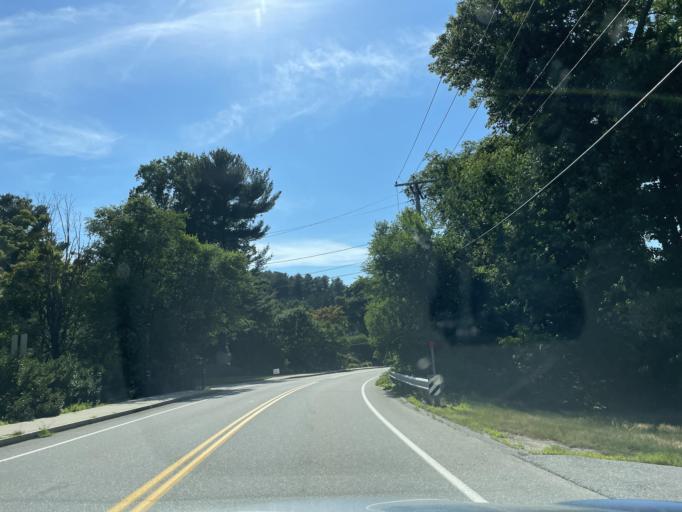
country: US
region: Massachusetts
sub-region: Worcester County
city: Northbridge
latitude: 42.1535
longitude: -71.6556
